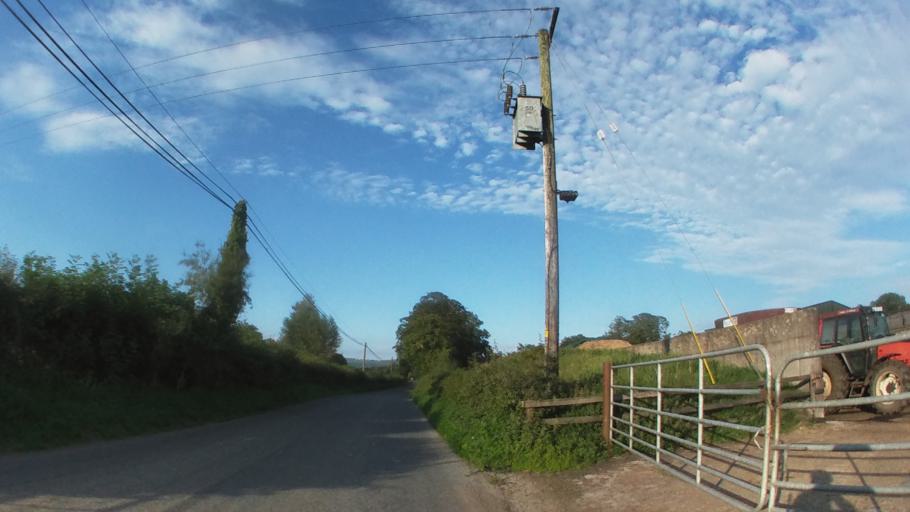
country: IE
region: Leinster
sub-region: Kilkenny
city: Kilkenny
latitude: 52.6712
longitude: -7.2099
